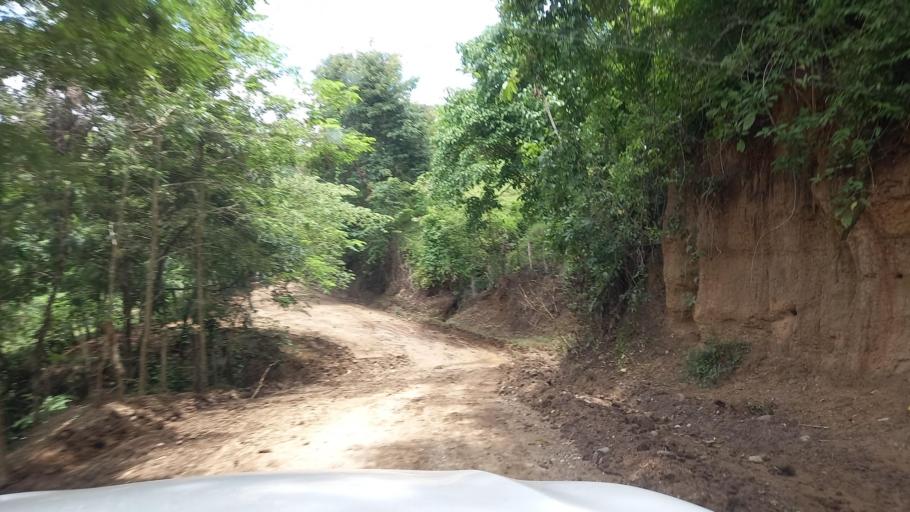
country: NI
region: Nueva Segovia
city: Wiwili
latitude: 13.7228
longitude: -85.7853
